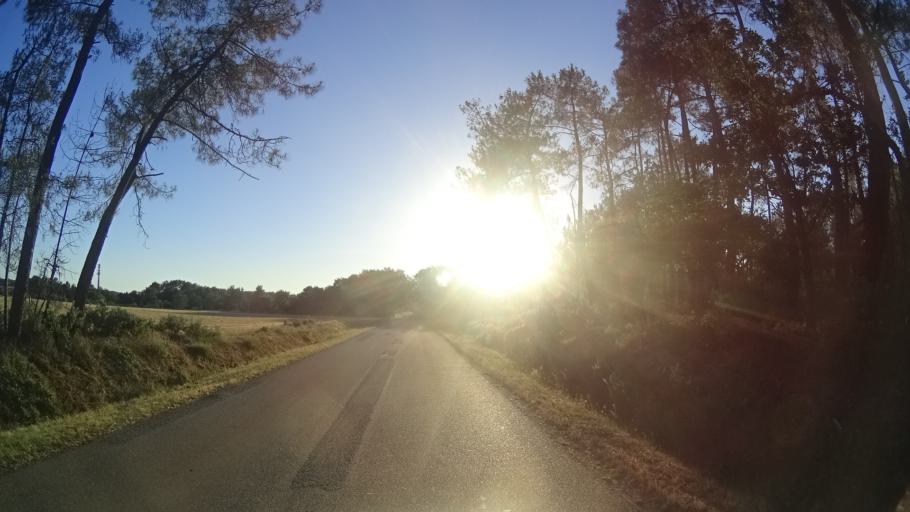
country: FR
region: Brittany
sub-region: Departement d'Ille-et-Vilaine
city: Langon
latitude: 47.7181
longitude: -1.8794
